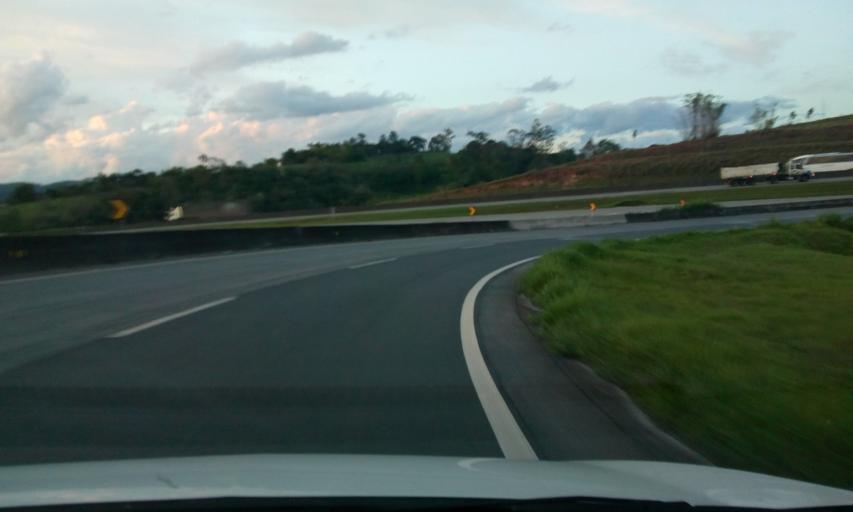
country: BR
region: Sao Paulo
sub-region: Jacarei
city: Jacarei
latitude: -23.3088
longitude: -46.0465
